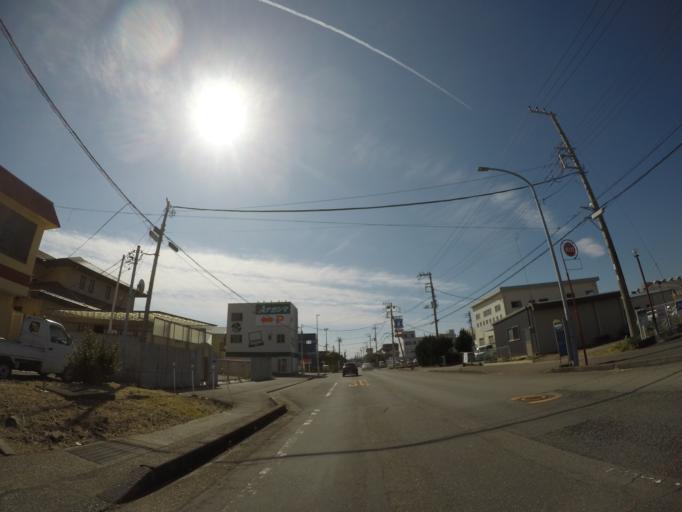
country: JP
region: Shizuoka
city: Numazu
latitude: 35.1170
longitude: 138.8324
